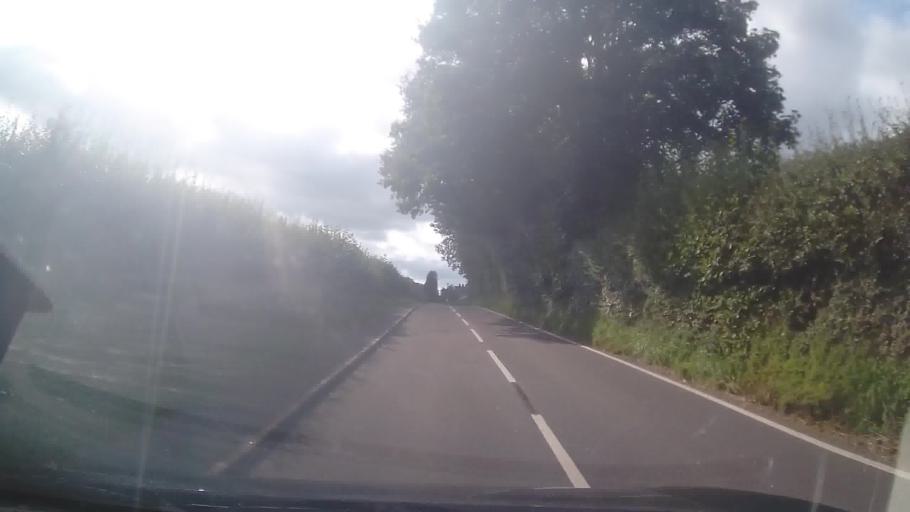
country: GB
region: England
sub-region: Shropshire
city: Bishop's Castle
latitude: 52.4966
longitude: -2.9906
